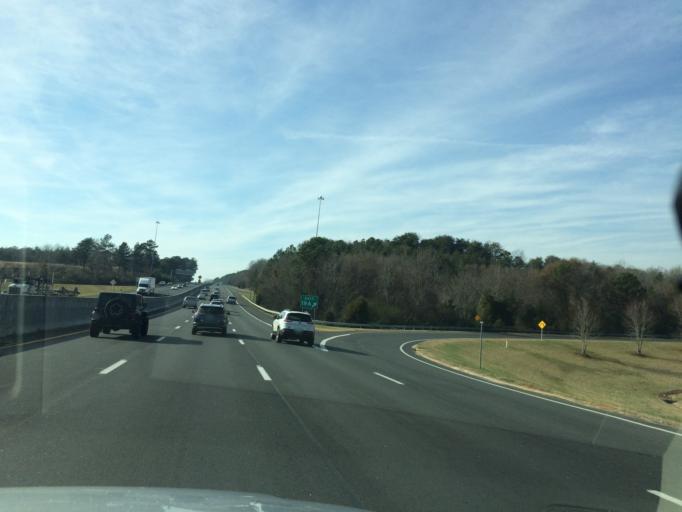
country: US
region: South Carolina
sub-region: Anderson County
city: Northlake
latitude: 34.5734
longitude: -82.7116
